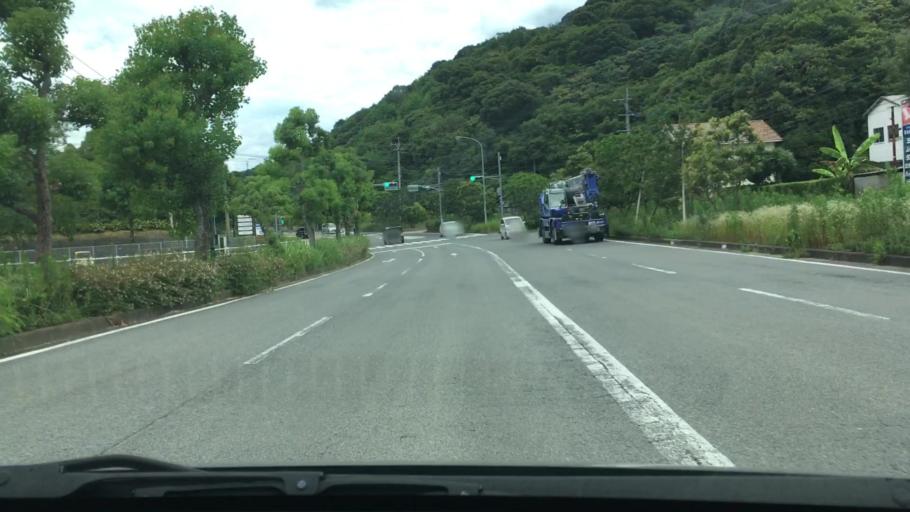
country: JP
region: Nagasaki
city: Sasebo
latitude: 32.9934
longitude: 129.7598
